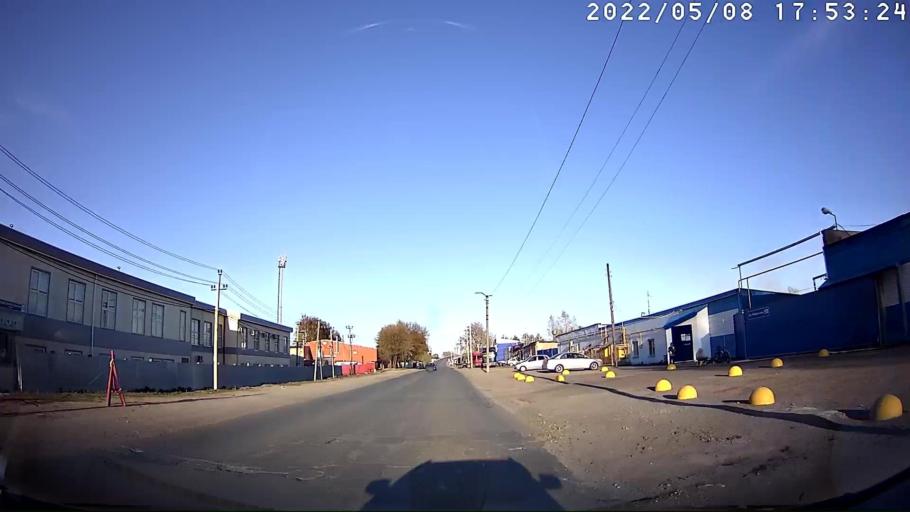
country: RU
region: Tatarstan
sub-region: Zelenodol'skiy Rayon
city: Zelenodolsk
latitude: 55.8396
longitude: 48.5174
